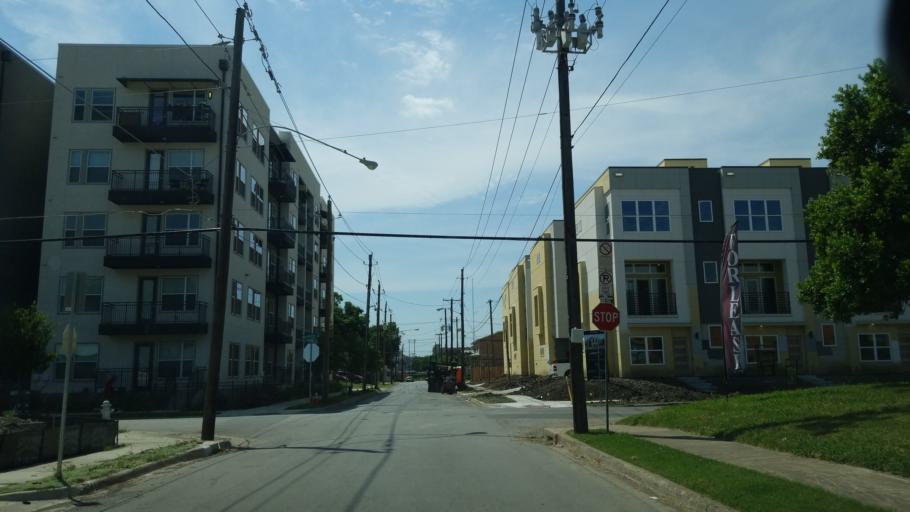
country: US
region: Texas
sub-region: Dallas County
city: Dallas
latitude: 32.7998
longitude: -96.7862
